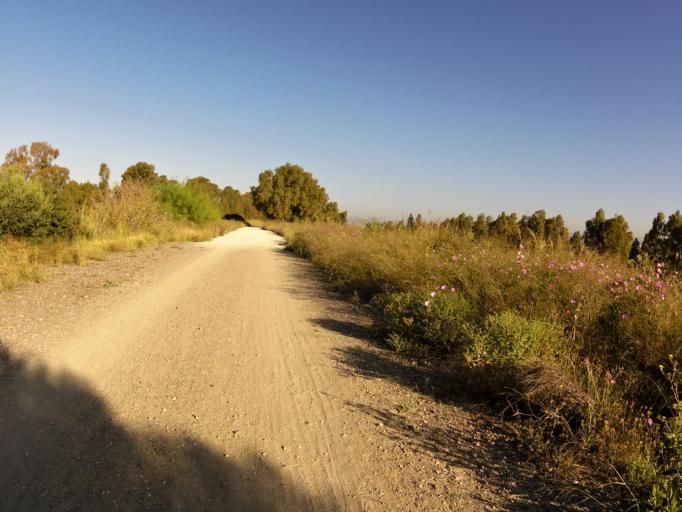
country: ES
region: Andalusia
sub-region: Provincia de Malaga
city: Torremolinos
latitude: 36.6739
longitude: -4.4675
